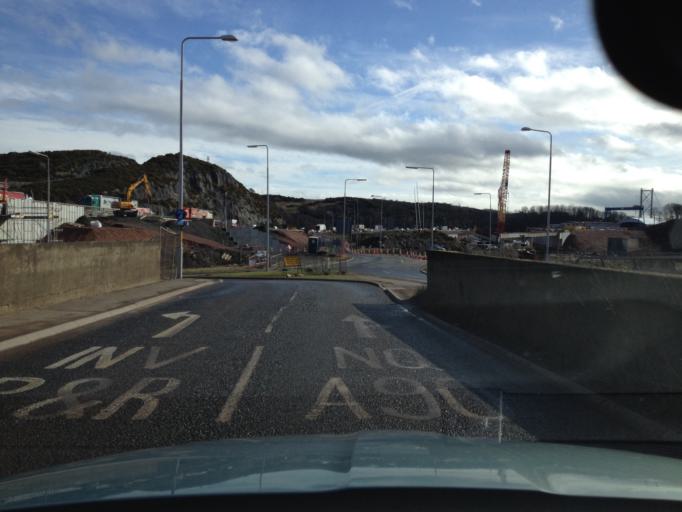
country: GB
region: Scotland
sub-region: Fife
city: Inverkeithing
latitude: 56.0212
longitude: -3.4082
